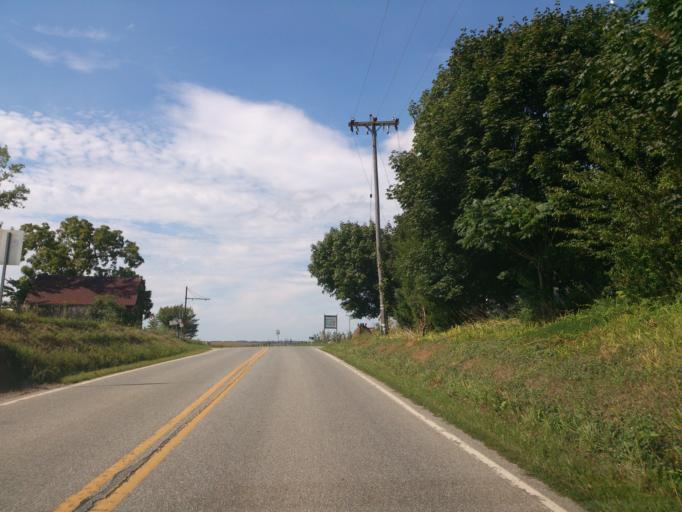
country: US
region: Pennsylvania
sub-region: York County
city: Susquehanna Trails
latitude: 39.7784
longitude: -76.4658
